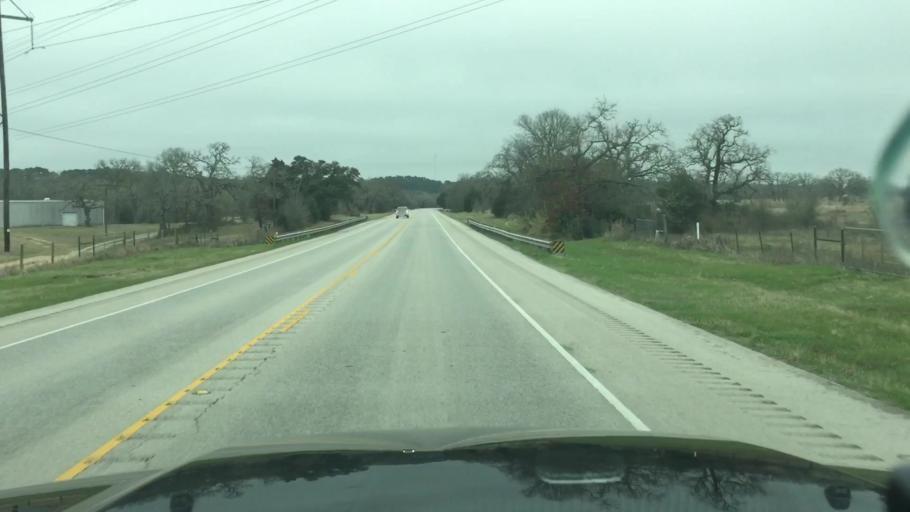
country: US
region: Texas
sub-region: Fayette County
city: La Grange
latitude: 30.0278
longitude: -96.9048
